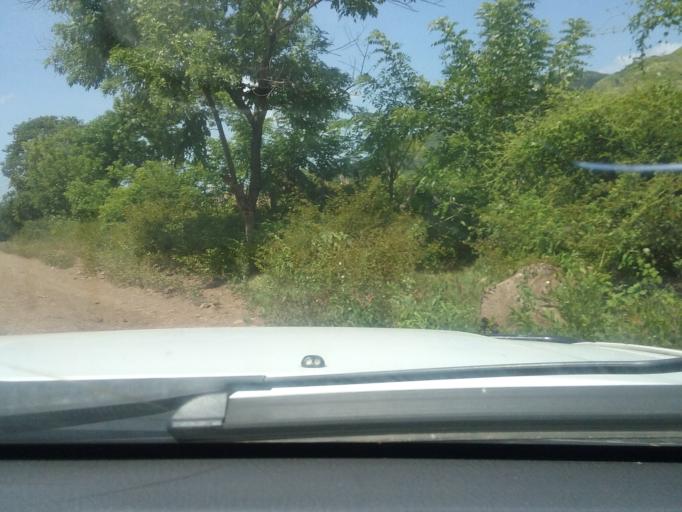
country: NI
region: Matagalpa
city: Terrabona
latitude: 12.6721
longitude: -85.9803
